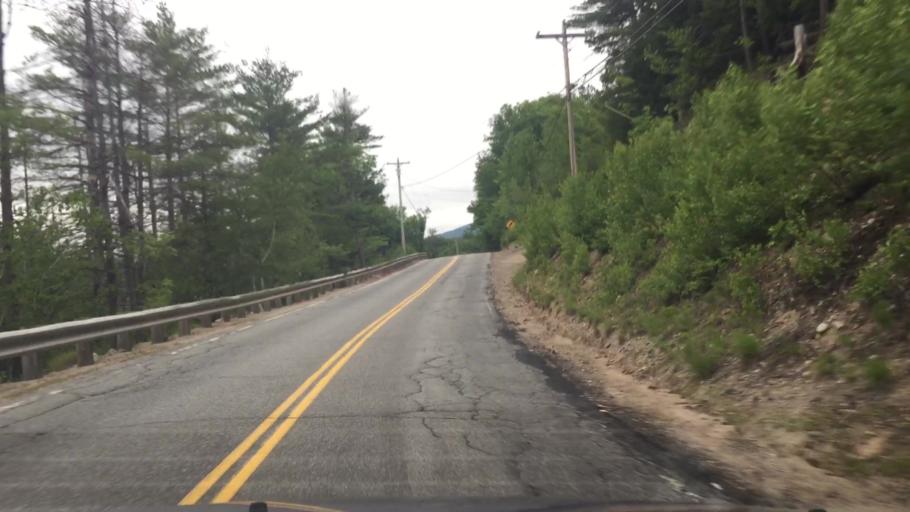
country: US
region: New Hampshire
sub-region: Carroll County
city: North Conway
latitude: 44.0964
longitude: -71.1990
